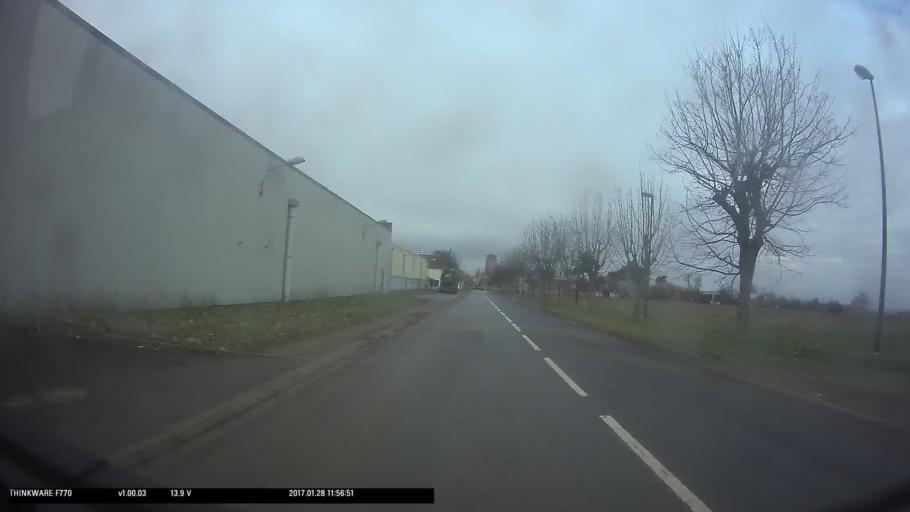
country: FR
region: Ile-de-France
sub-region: Departement du Val-d'Oise
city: Vigny
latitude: 49.0853
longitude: 1.9252
